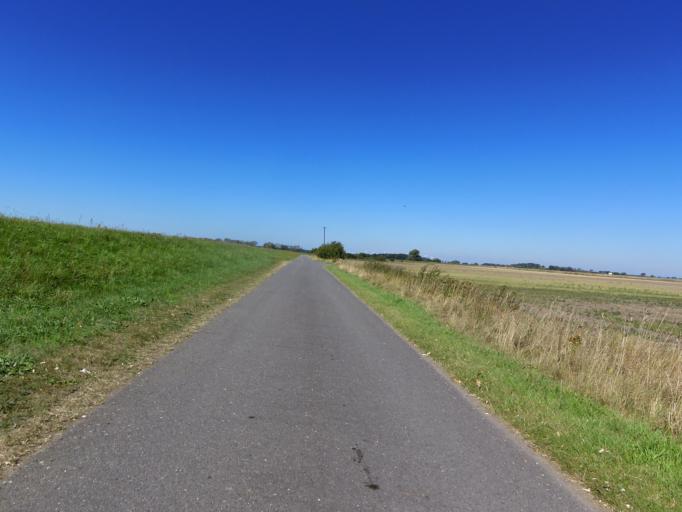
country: DE
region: Saxony-Anhalt
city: Pretzsch
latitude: 51.7215
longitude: 12.8170
